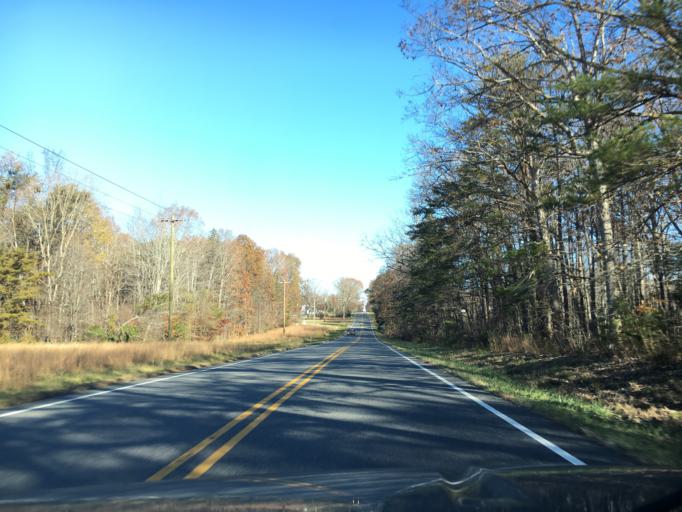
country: US
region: Virginia
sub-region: Appomattox County
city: Appomattox
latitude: 37.4382
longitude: -78.7199
